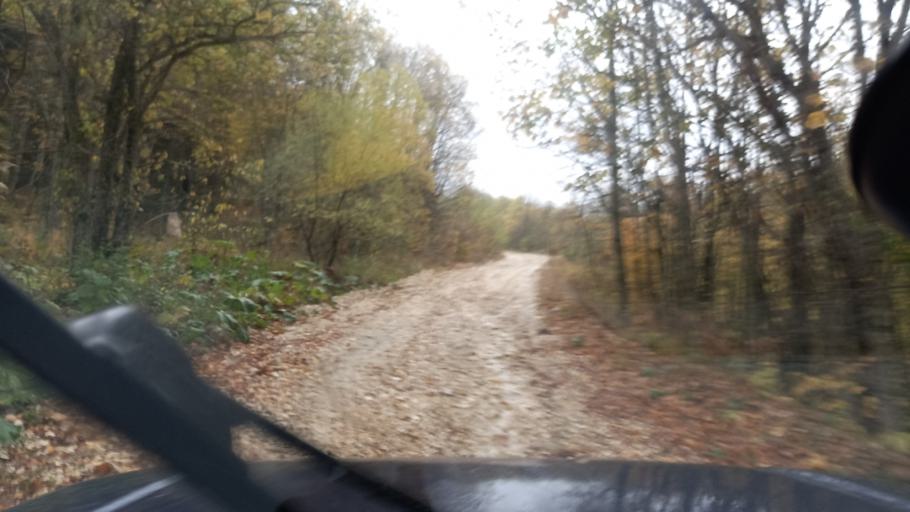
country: RU
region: Krasnodarskiy
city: Neftegorsk
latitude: 44.0238
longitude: 39.8382
